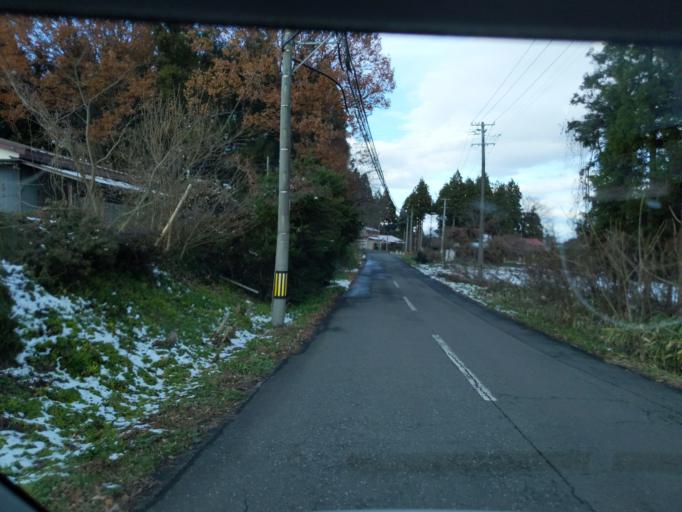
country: JP
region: Iwate
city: Kitakami
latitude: 39.2095
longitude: 141.0495
